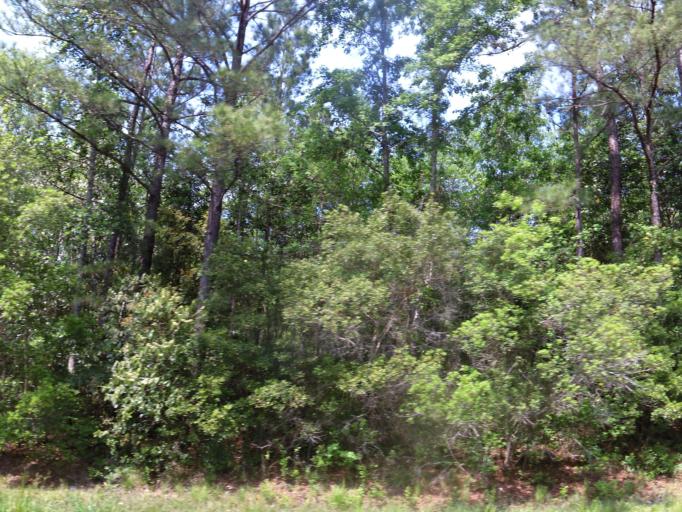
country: US
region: Georgia
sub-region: Camden County
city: Kingsland
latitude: 30.8013
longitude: -81.7291
